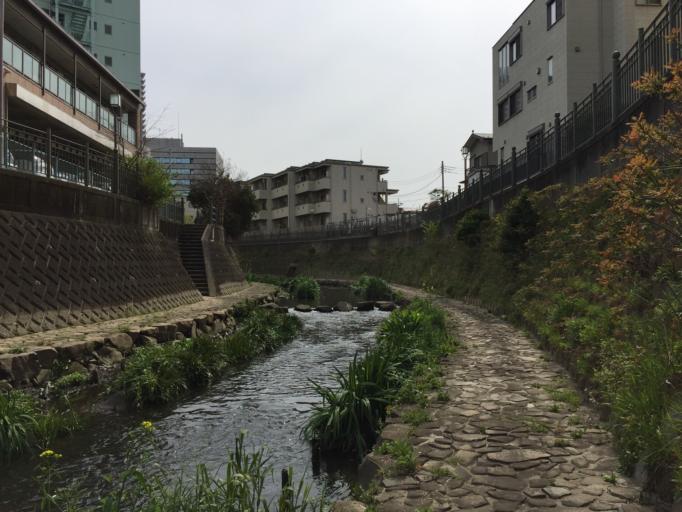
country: JP
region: Kanagawa
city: Yokohama
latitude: 35.4122
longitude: 139.5963
